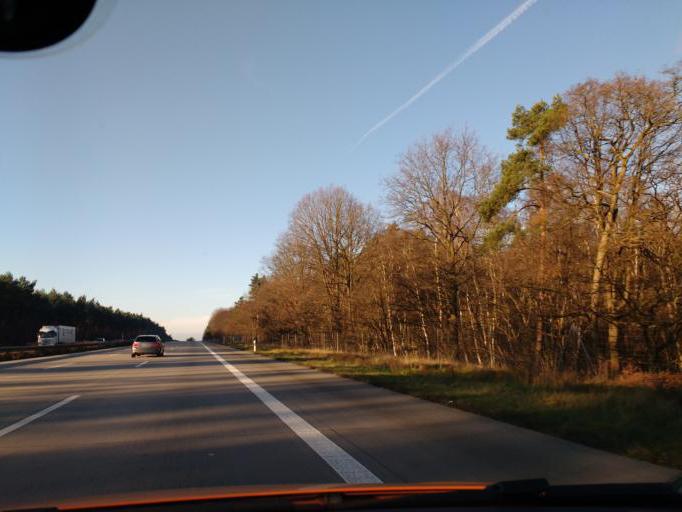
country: DE
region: Saxony-Anhalt
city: Mockern
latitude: 52.2338
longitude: 12.0306
